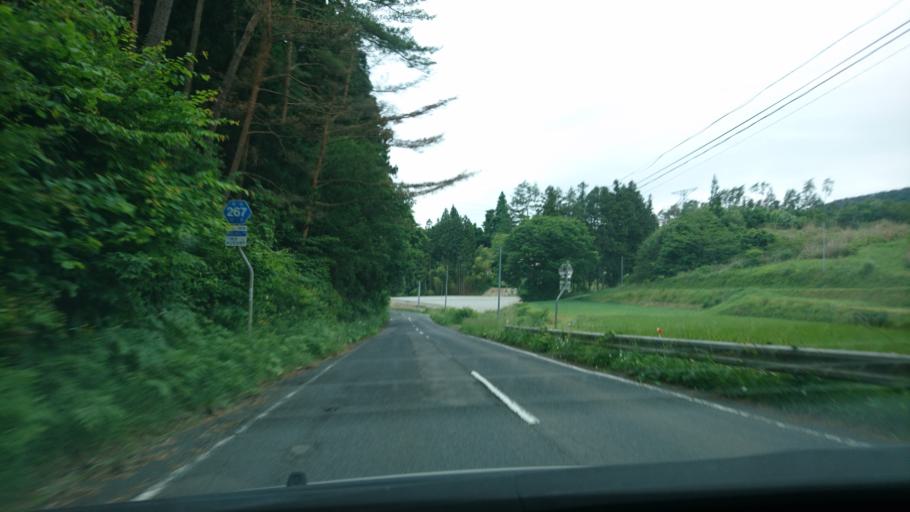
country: JP
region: Iwate
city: Ichinoseki
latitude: 38.9470
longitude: 141.2690
